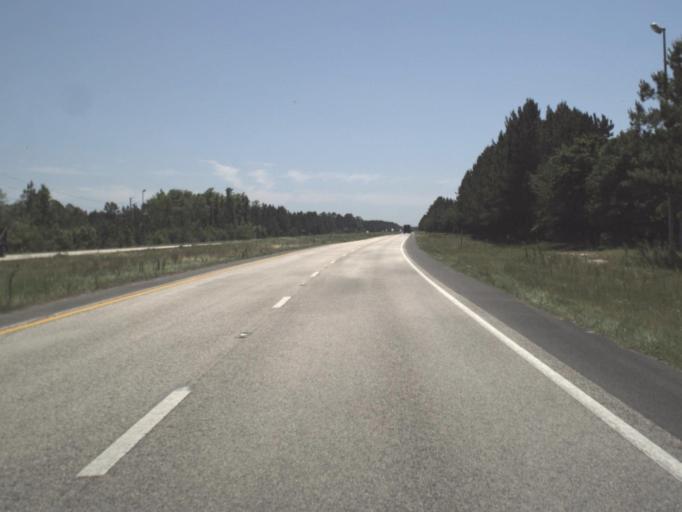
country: US
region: Florida
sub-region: Clay County
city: Bellair-Meadowbrook Terrace
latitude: 30.2154
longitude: -81.8376
